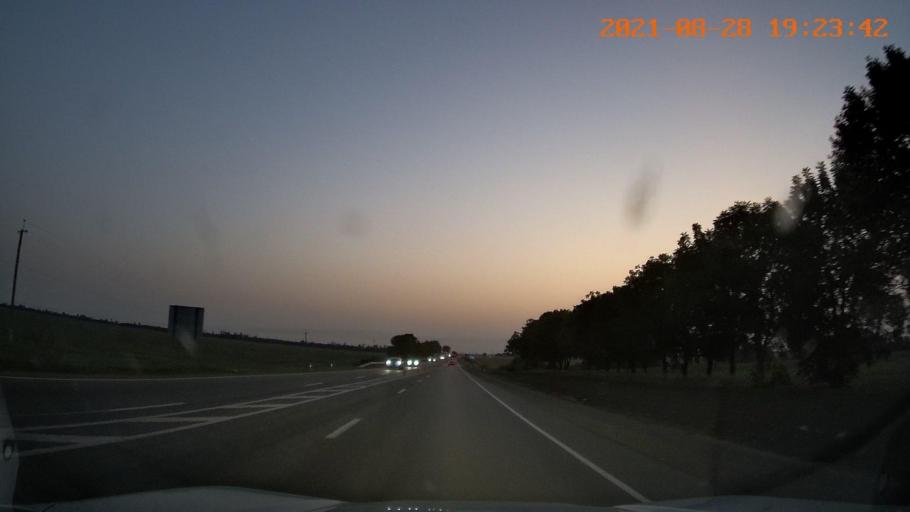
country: RU
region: Adygeya
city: Ponezhukay
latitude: 44.8740
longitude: 39.4460
